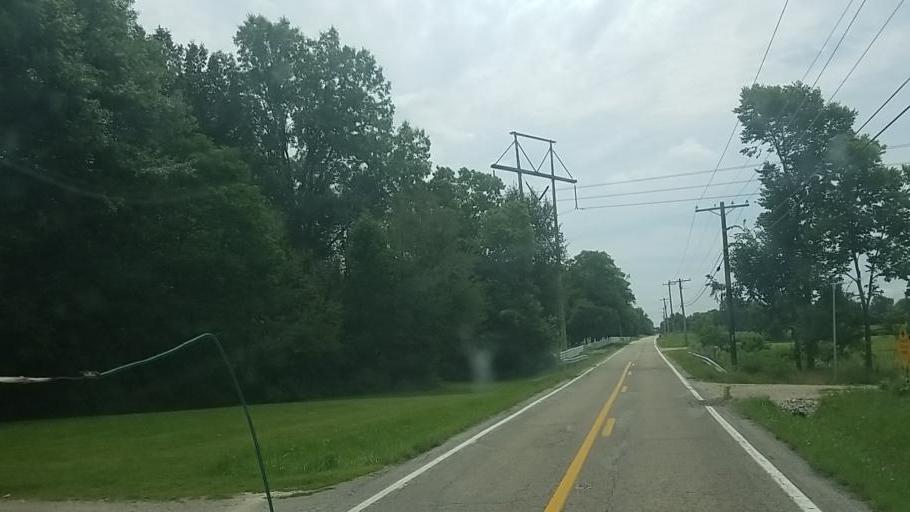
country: US
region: Ohio
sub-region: Franklin County
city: New Albany
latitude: 40.1197
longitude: -82.8207
